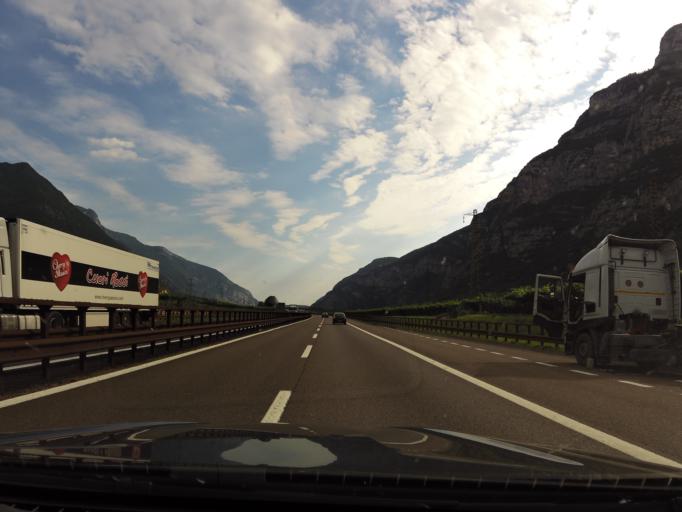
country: IT
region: Veneto
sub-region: Provincia di Verona
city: Rivalta
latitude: 45.6374
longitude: 10.8755
